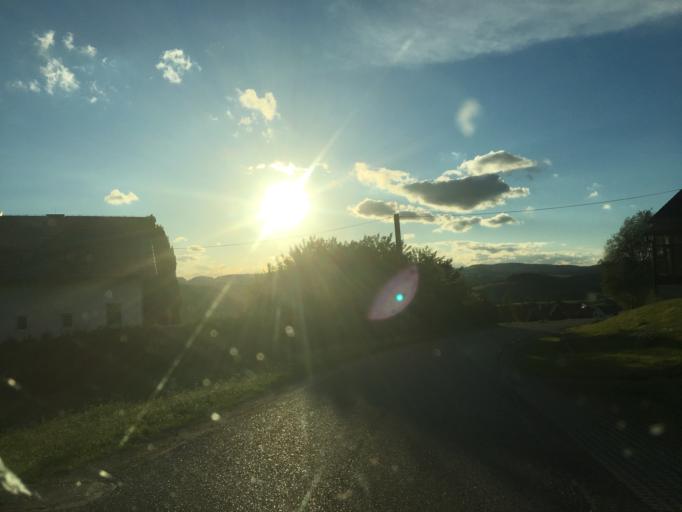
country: AT
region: Upper Austria
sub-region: Politischer Bezirk Urfahr-Umgebung
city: Zwettl an der Rodl
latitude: 48.4599
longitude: 14.2856
